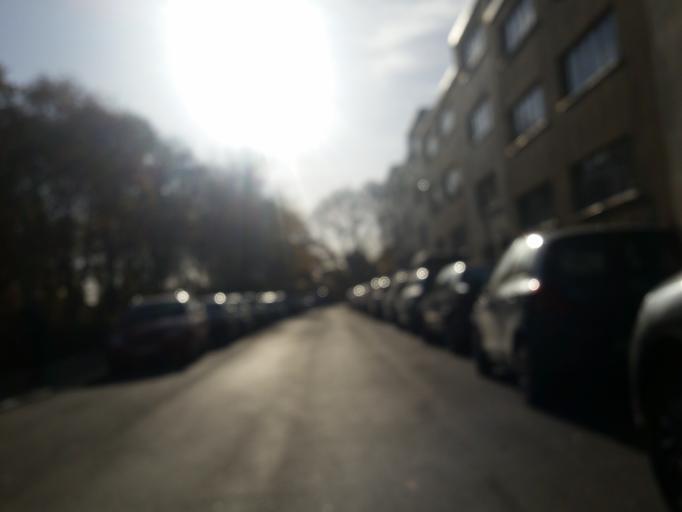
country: SE
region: Stockholm
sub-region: Stockholms Kommun
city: Arsta
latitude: 59.3069
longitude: 18.0716
